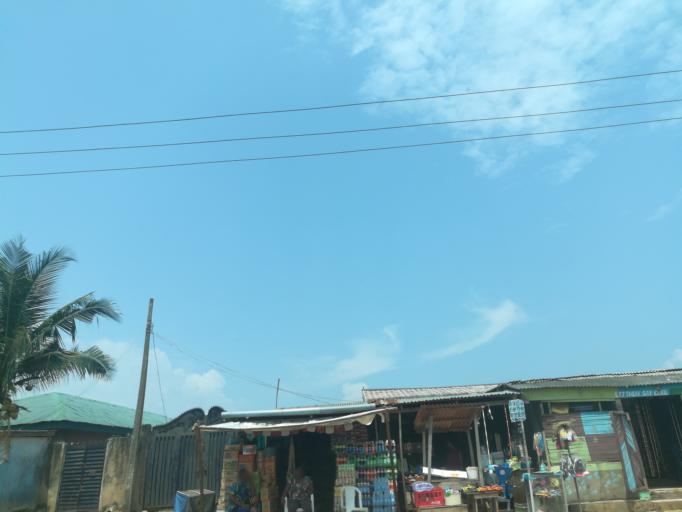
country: NG
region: Lagos
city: Ikorodu
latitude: 6.5811
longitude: 3.6266
